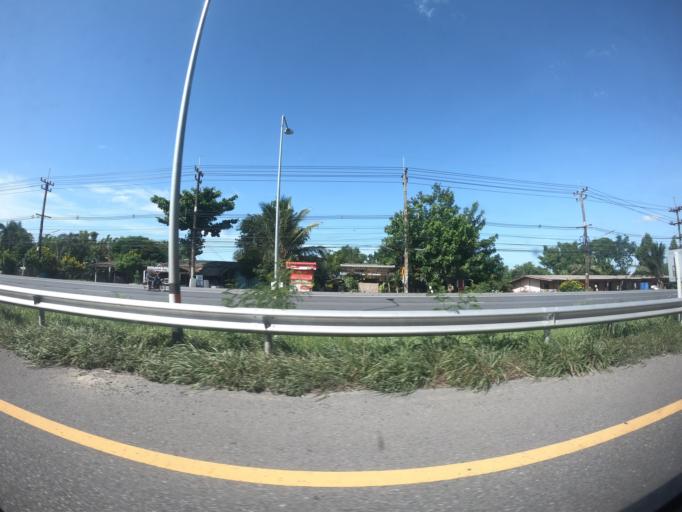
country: TH
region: Nakhon Nayok
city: Ban Na
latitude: 14.2435
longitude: 101.1133
